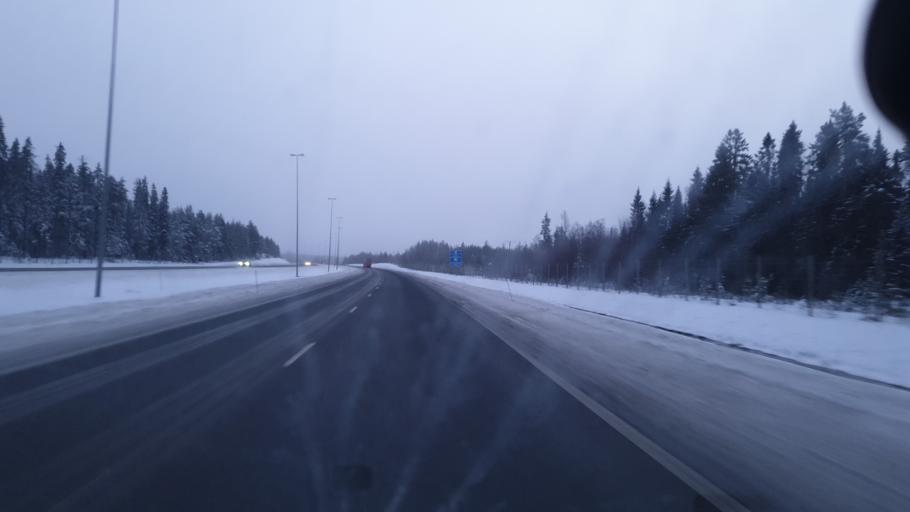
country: FI
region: Lapland
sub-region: Kemi-Tornio
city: Keminmaa
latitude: 65.8278
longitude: 24.3791
